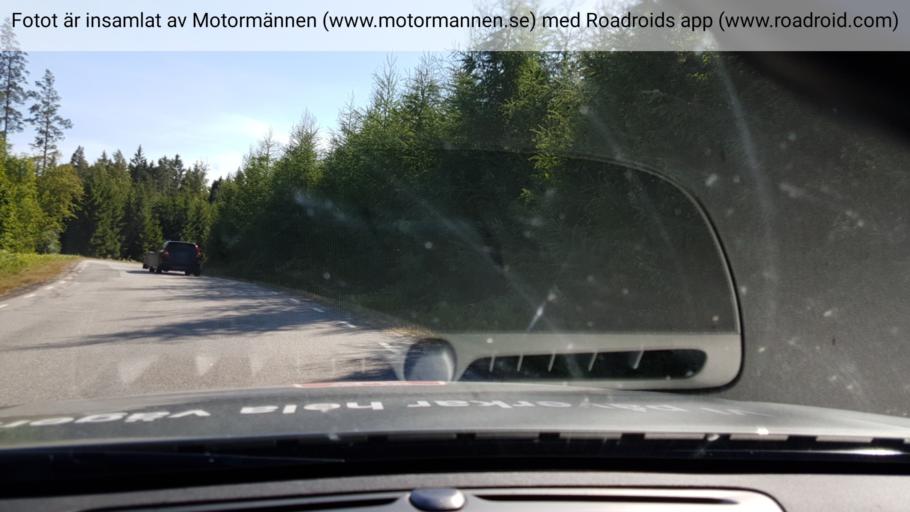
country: SE
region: Vaestra Goetaland
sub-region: Toreboda Kommun
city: Toereboda
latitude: 58.6651
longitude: 14.2828
